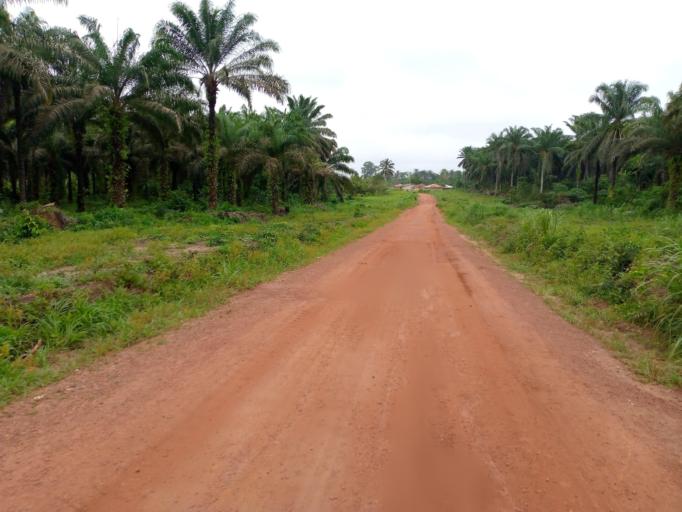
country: SL
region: Southern Province
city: Sumbuya
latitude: 7.5991
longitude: -12.0837
